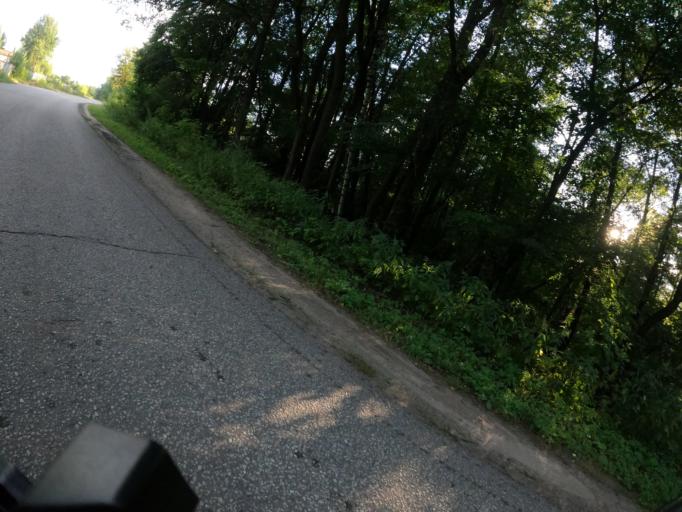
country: RU
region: Moskovskaya
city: Beloozerskiy
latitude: 55.4596
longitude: 38.4831
